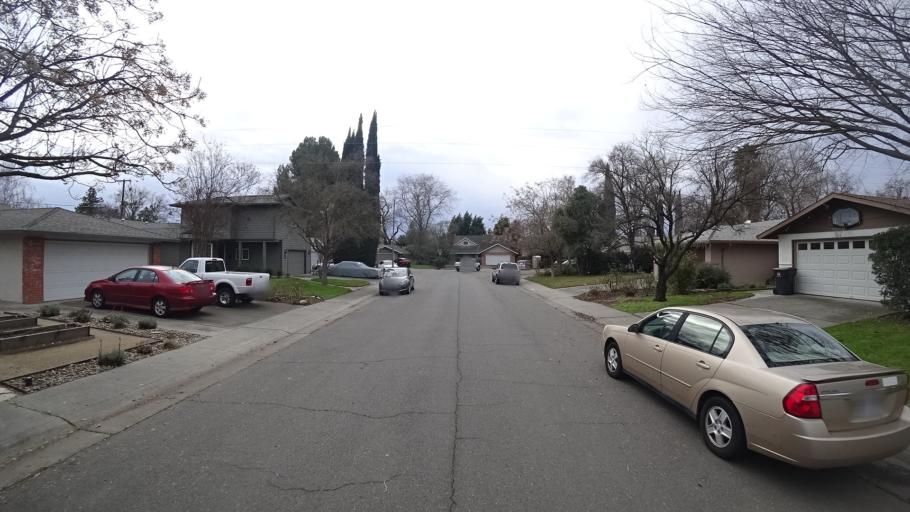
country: US
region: California
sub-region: Yolo County
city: Davis
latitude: 38.5595
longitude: -121.7238
